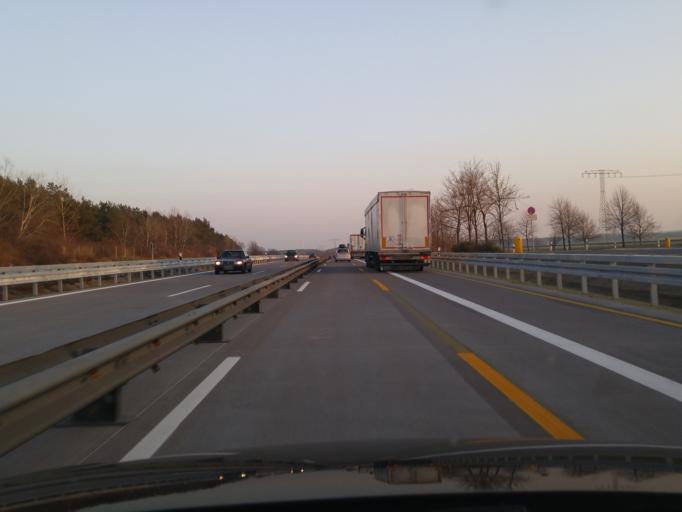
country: DE
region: Brandenburg
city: Golzow
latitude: 52.3385
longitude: 12.6454
